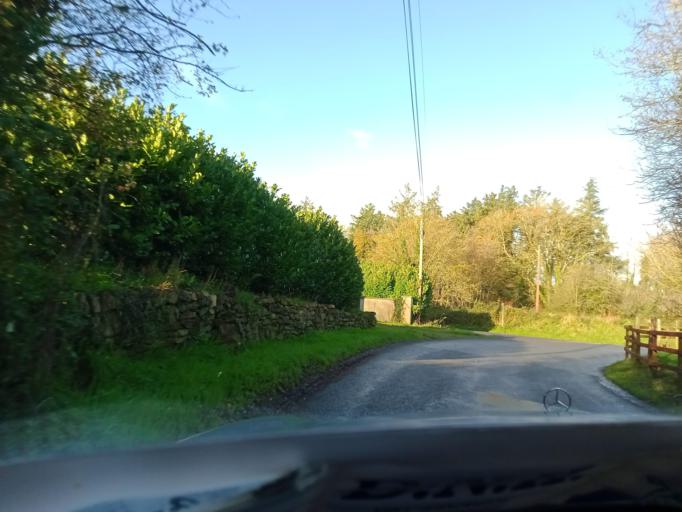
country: IE
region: Leinster
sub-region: Kilkenny
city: Mooncoin
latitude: 52.2769
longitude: -7.2370
